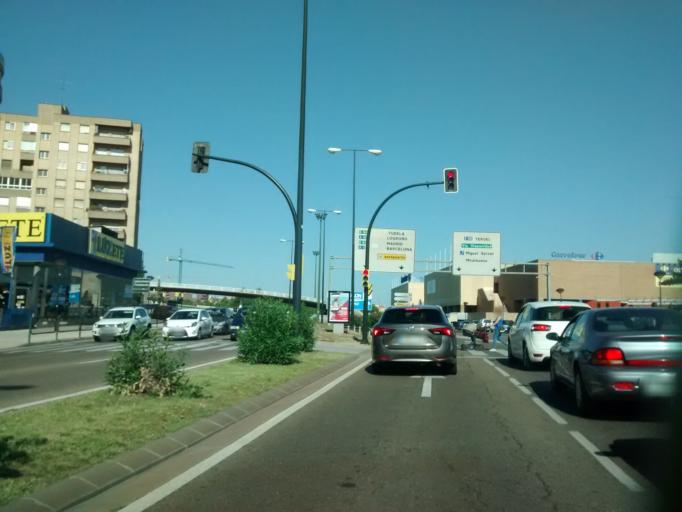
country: ES
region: Aragon
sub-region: Provincia de Zaragoza
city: Delicias
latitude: 41.6587
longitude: -0.9192
